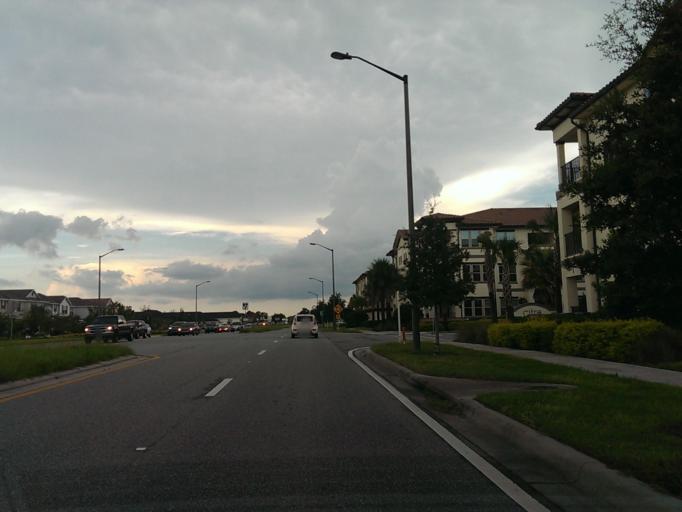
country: US
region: Florida
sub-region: Orange County
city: Bay Hill
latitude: 28.4420
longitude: -81.5598
